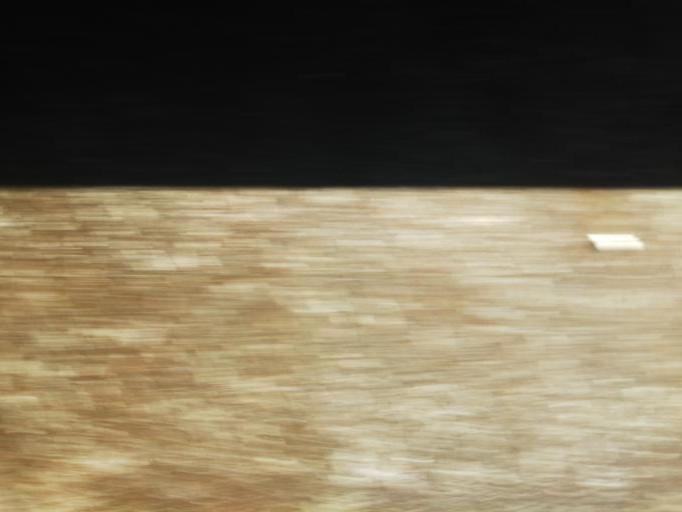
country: JP
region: Kochi
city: Nakamura
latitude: 33.0875
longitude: 133.1023
